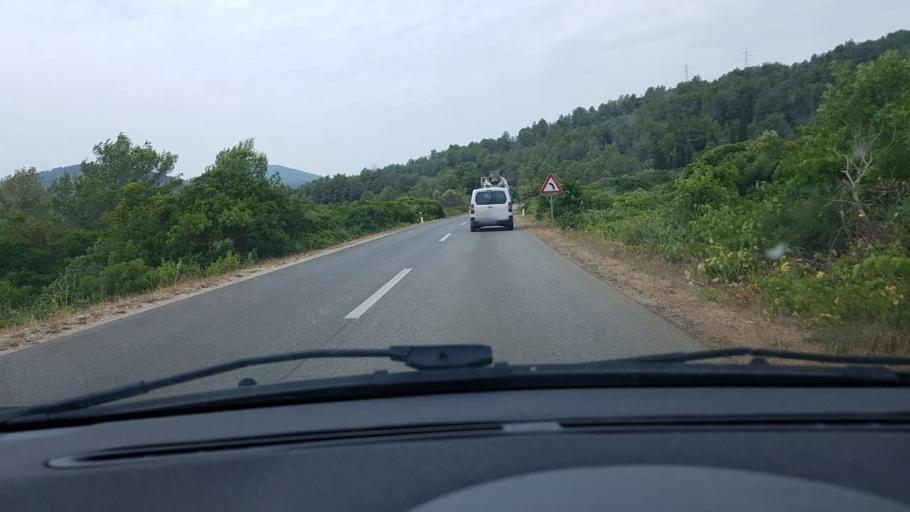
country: HR
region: Dubrovacko-Neretvanska
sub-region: Grad Dubrovnik
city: Vela Luka
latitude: 42.9508
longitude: 16.7527
